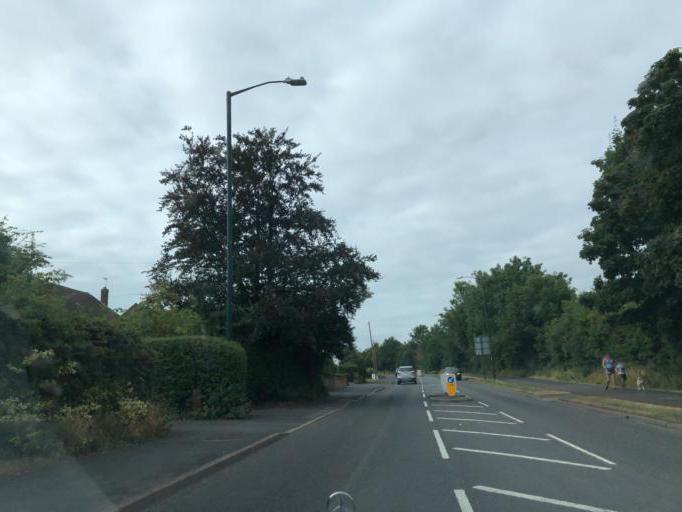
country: GB
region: England
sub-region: Warwickshire
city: Royal Leamington Spa
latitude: 52.2672
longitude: -1.5346
